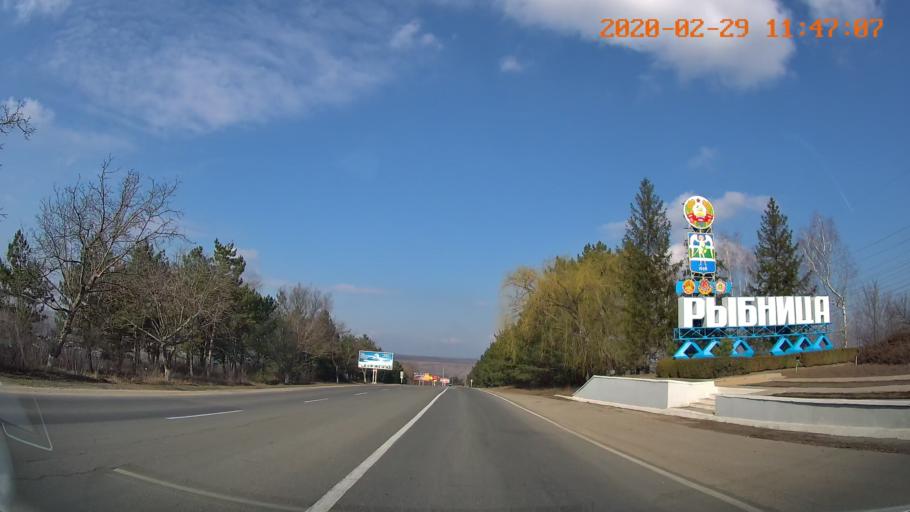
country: MD
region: Rezina
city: Rezina
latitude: 47.7379
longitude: 28.9901
